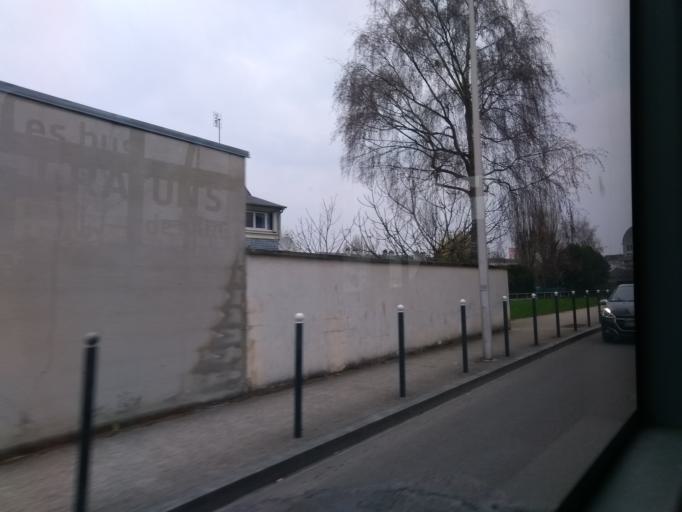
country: FR
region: Picardie
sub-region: Departement de l'Oise
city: Venette
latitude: 49.4054
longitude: 2.8015
